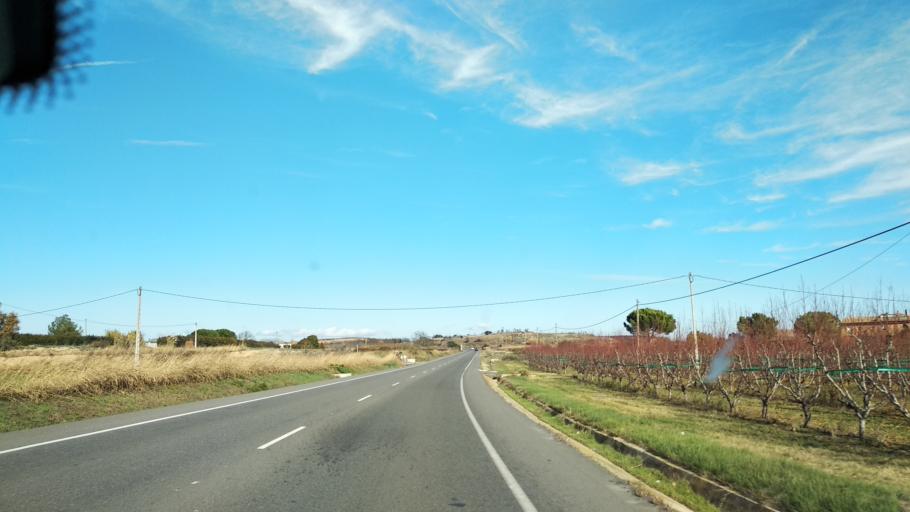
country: ES
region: Catalonia
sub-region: Provincia de Lleida
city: Alcoletge
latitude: 41.6642
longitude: 0.6643
